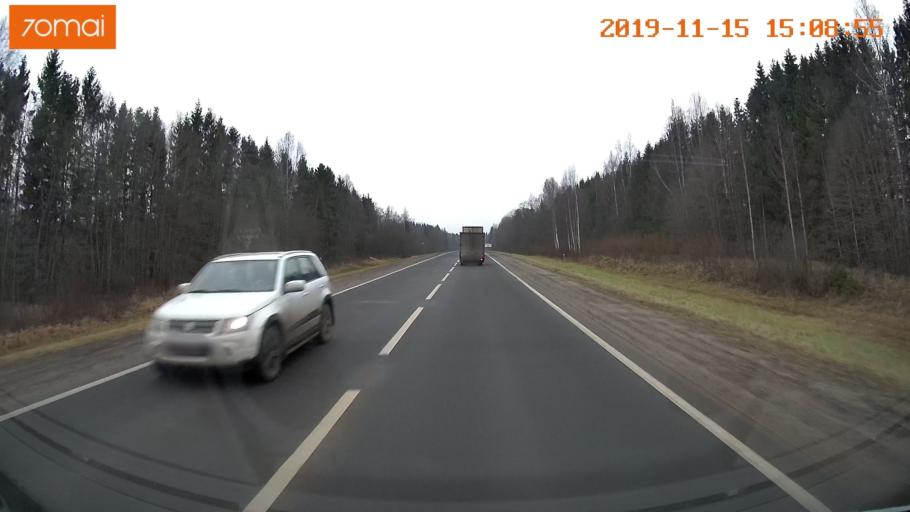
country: RU
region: Jaroslavl
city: Prechistoye
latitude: 58.3643
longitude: 40.2706
